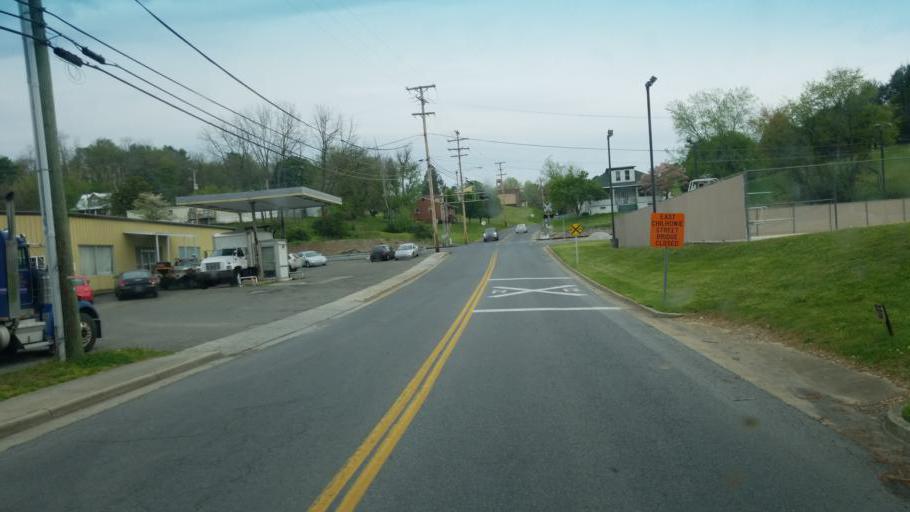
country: US
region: Virginia
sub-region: Smyth County
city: Marion
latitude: 36.8377
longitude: -81.5168
